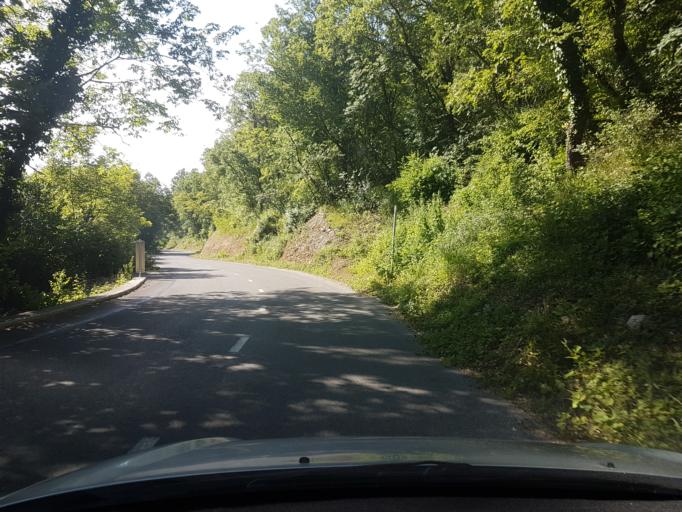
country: SI
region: Divaca
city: Divaca
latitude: 45.7548
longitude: 13.9405
